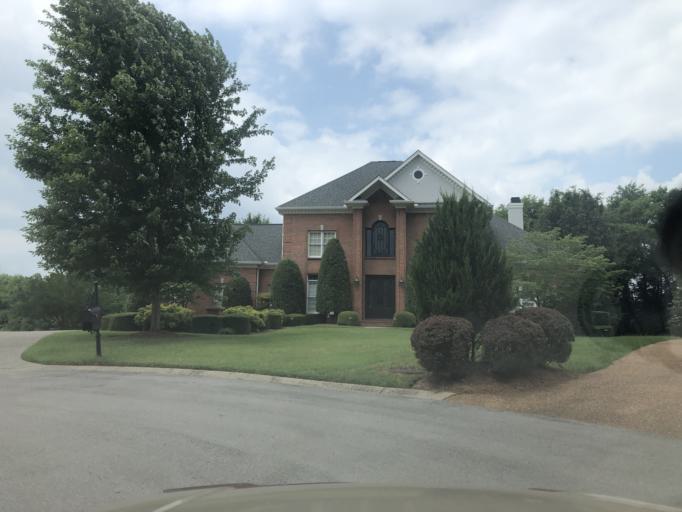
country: US
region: Tennessee
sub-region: Davidson County
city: Lakewood
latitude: 36.2402
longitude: -86.6079
